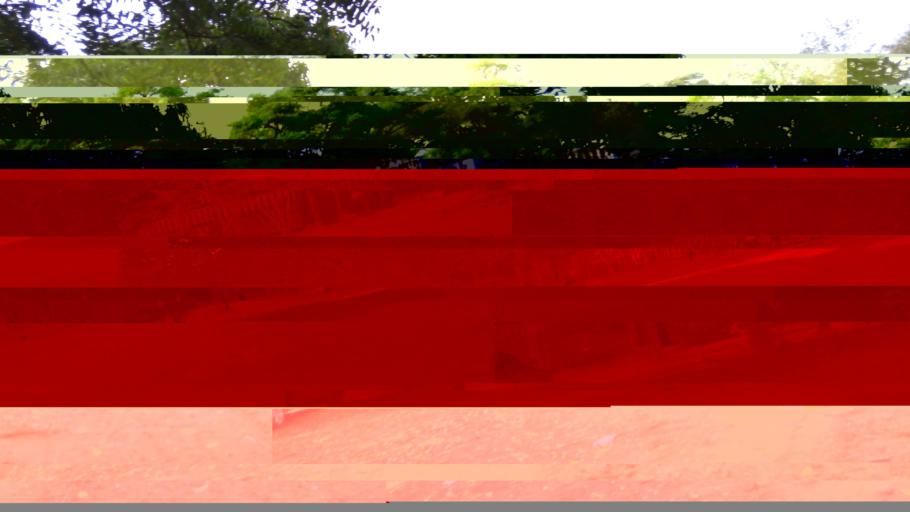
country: TG
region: Maritime
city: Lome
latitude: 6.1761
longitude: 1.2133
